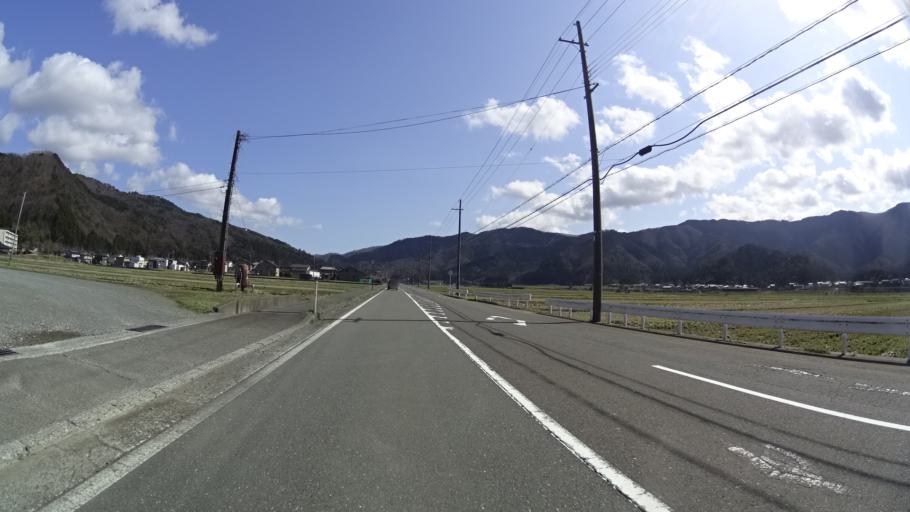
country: JP
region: Fukui
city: Obama
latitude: 35.4618
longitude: 135.8731
